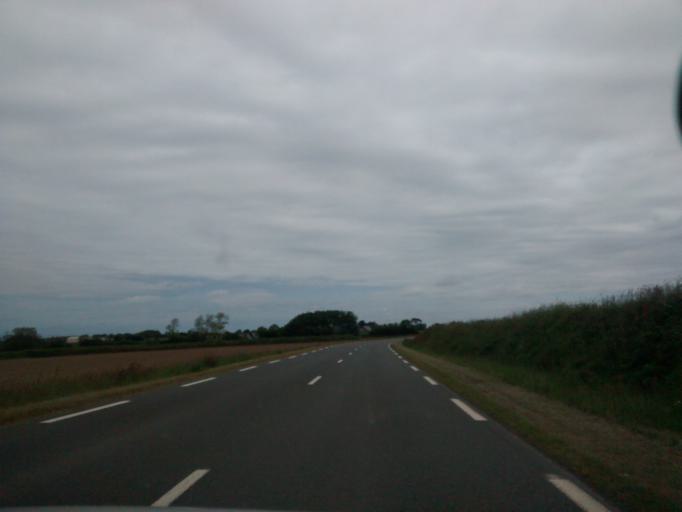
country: FR
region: Brittany
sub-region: Departement des Cotes-d'Armor
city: Penvenan
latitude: 48.7917
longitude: -3.3196
